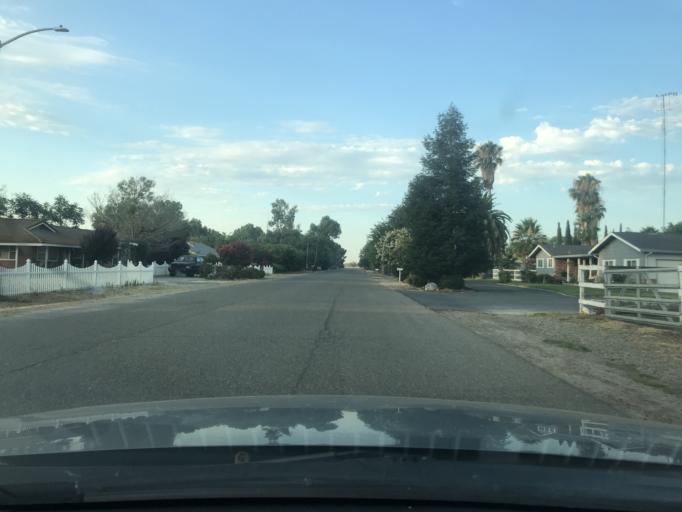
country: US
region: California
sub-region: Merced County
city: Merced
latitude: 37.3292
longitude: -120.5378
